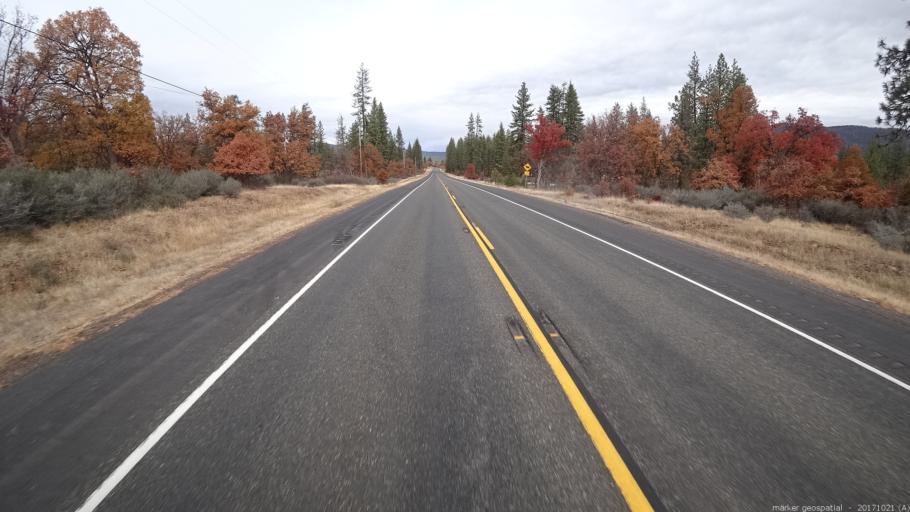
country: US
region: California
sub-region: Shasta County
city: Burney
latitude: 41.0361
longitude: -121.6298
